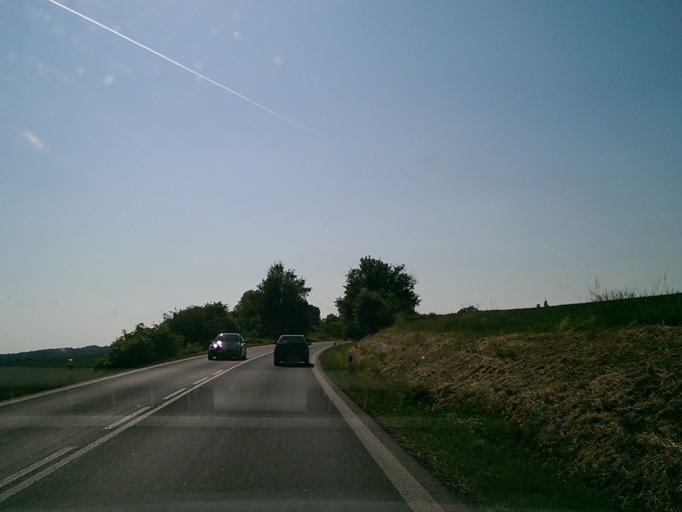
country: CZ
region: Liberecky
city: Rovensko pod Troskami
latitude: 50.5067
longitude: 15.2729
